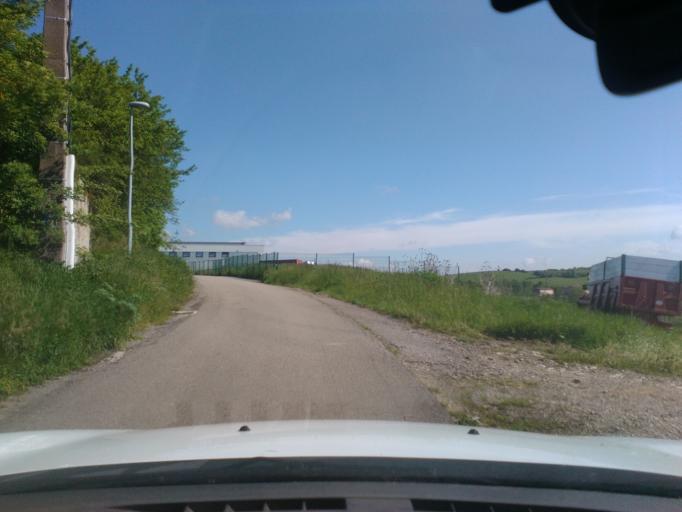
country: FR
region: Lorraine
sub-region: Departement des Vosges
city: Mirecourt
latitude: 48.3283
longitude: 6.1457
